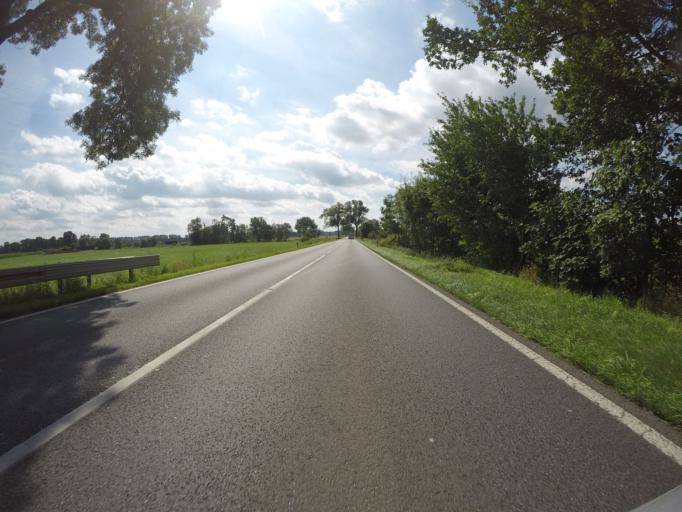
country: DE
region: Brandenburg
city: Oranienburg
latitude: 52.8426
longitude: 13.1956
